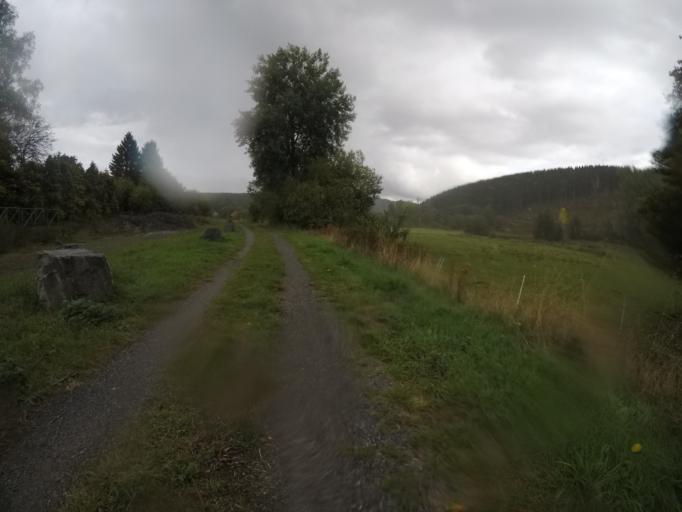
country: BE
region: Wallonia
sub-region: Province du Luxembourg
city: Fauvillers
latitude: 49.8755
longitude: 5.6776
